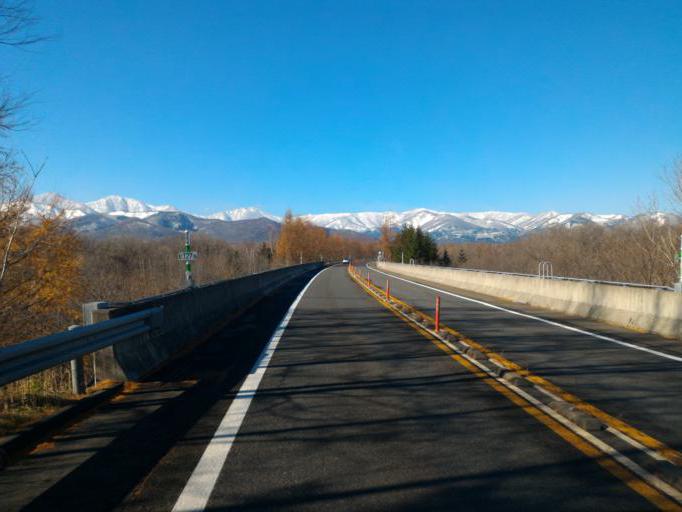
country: JP
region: Hokkaido
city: Otofuke
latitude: 42.9707
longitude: 142.8923
